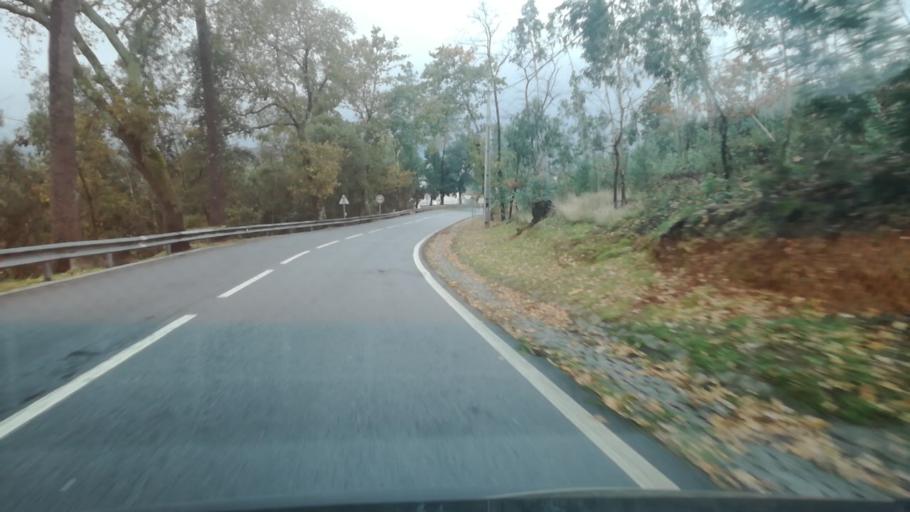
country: PT
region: Braga
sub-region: Braga
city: Braga
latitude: 41.5293
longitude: -8.3932
